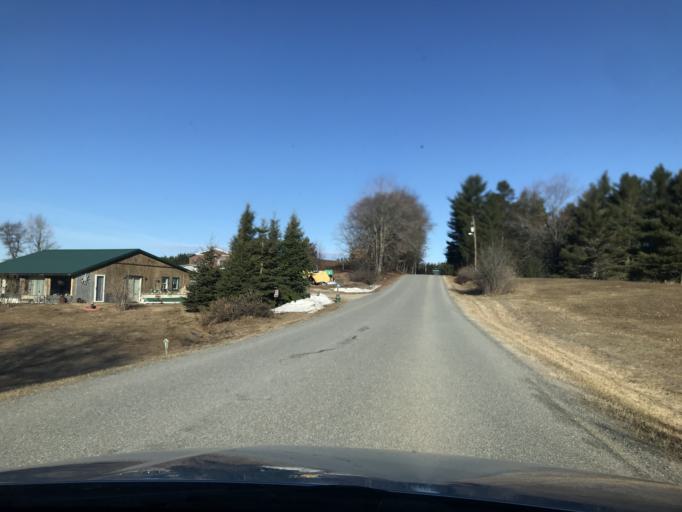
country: US
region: Wisconsin
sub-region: Marinette County
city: Niagara
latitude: 45.3886
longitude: -88.0474
